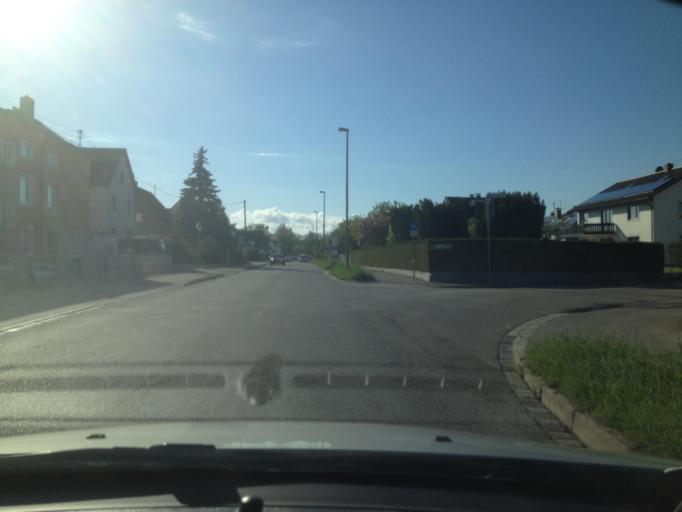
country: DE
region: Bavaria
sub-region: Swabia
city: Bobingen
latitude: 48.3133
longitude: 10.8538
